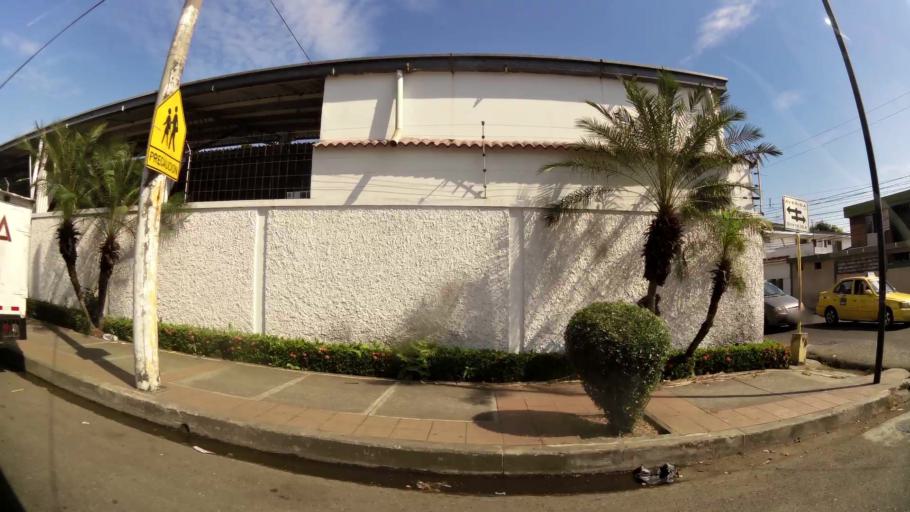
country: EC
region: Guayas
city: Guayaquil
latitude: -2.2205
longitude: -79.8938
